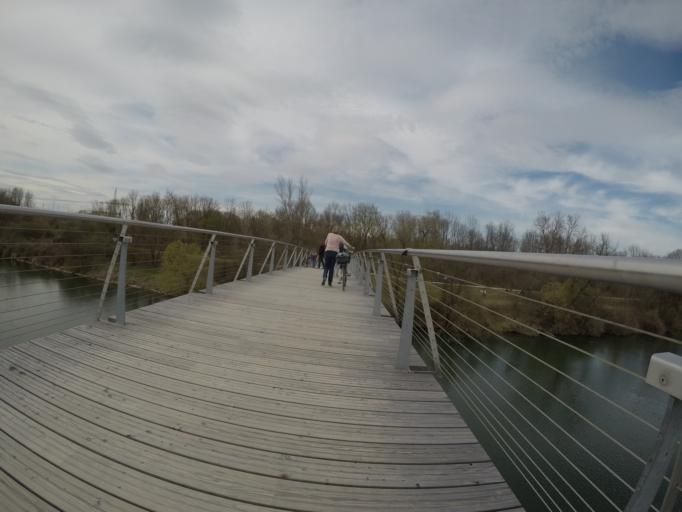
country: DE
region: Bavaria
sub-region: Lower Bavaria
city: Stallwang
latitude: 48.5843
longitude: 12.2265
